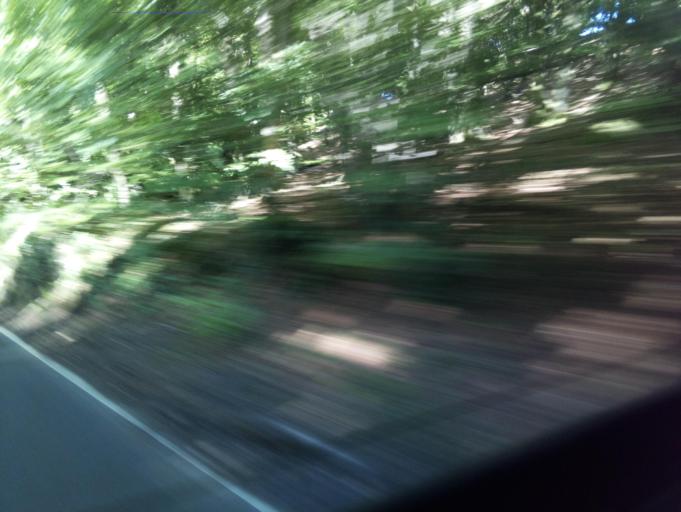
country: GB
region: England
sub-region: Dorset
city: Lyme Regis
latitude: 50.7884
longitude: -2.8949
